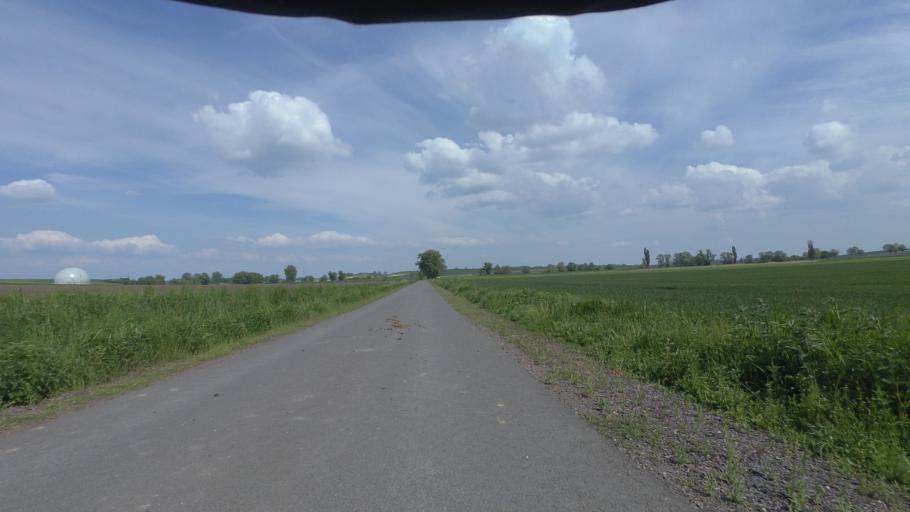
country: DE
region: Lower Saxony
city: Sollingen
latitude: 52.0987
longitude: 10.9331
